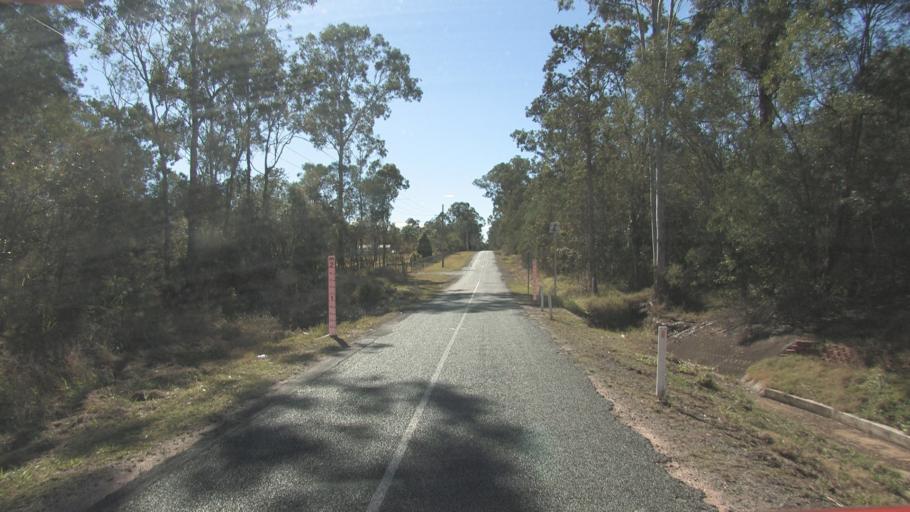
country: AU
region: Queensland
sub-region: Logan
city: Chambers Flat
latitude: -27.7978
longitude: 153.0707
